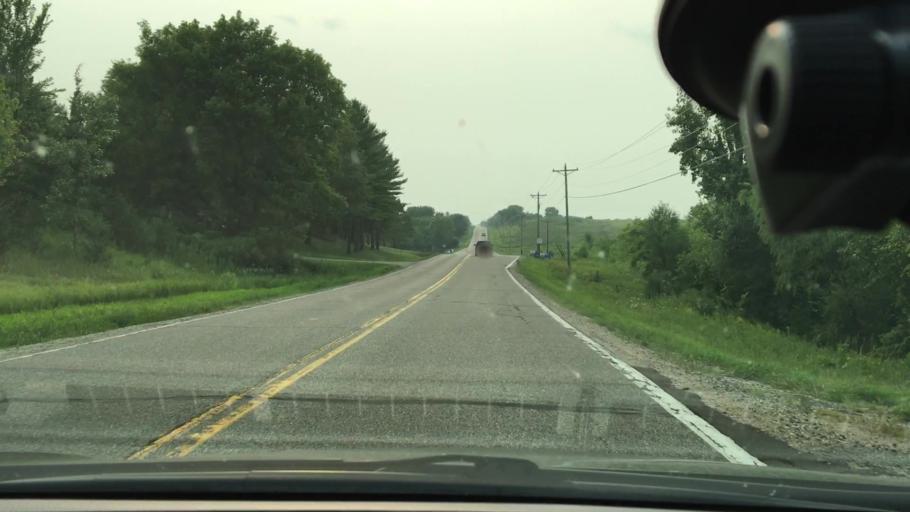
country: US
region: Minnesota
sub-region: Wright County
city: Otsego
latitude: 45.2525
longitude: -93.5616
